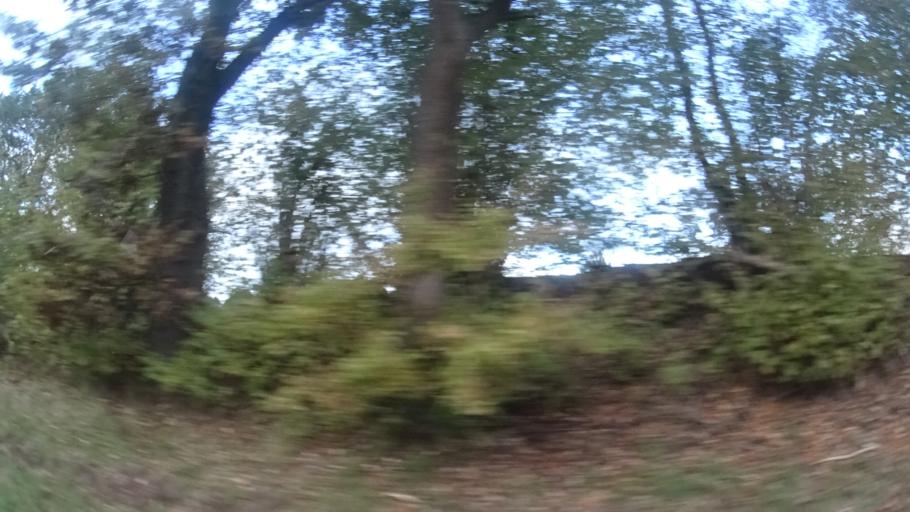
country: DE
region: Hesse
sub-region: Regierungsbezirk Kassel
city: Flieden
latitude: 50.4544
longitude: 9.5574
